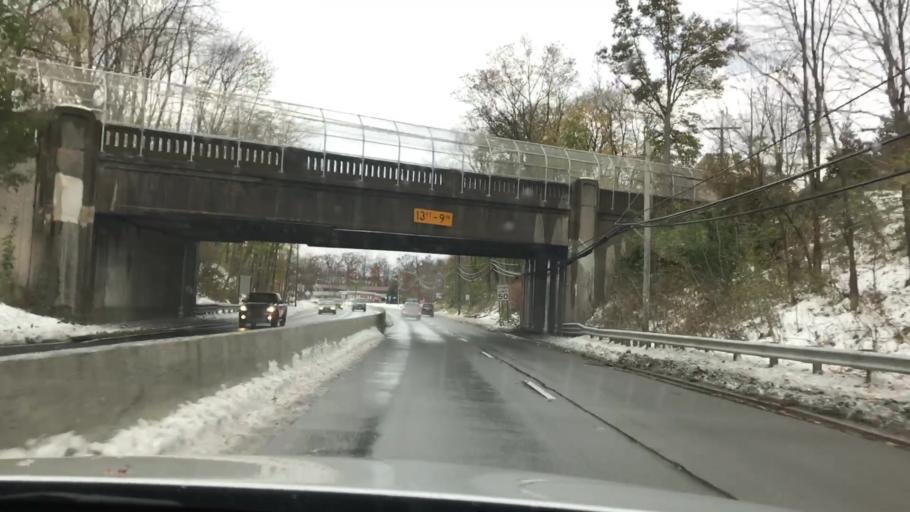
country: US
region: New Jersey
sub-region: Morris County
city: Parsippany
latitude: 40.8244
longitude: -74.4177
